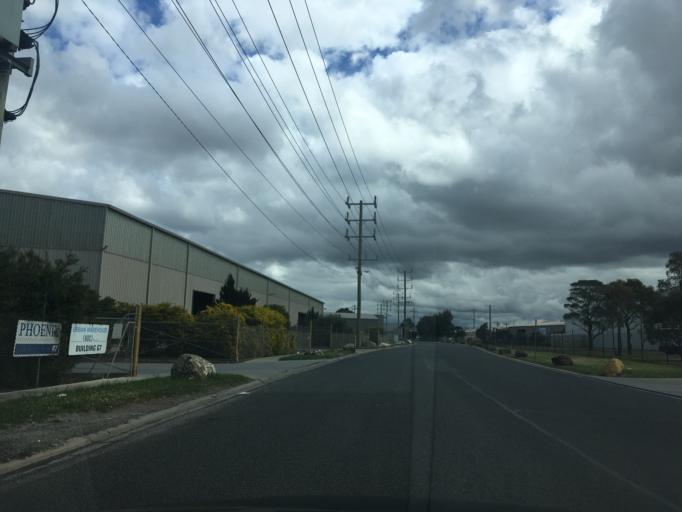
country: AU
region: Victoria
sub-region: Brimbank
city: Derrimut
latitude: -37.8215
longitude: 144.7899
